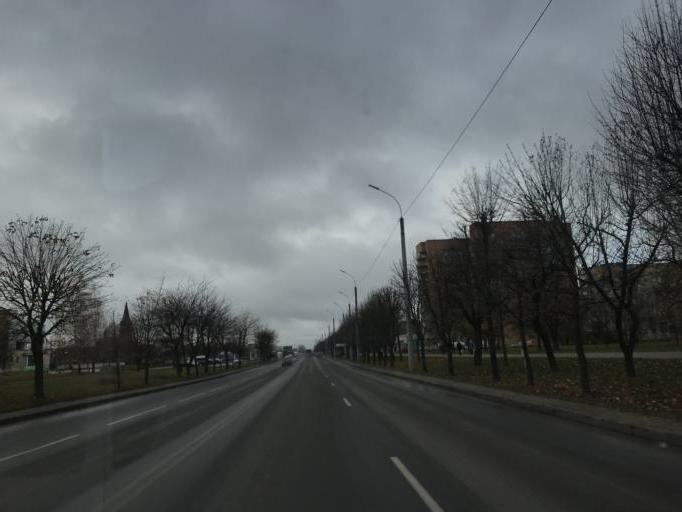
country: BY
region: Mogilev
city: Mahilyow
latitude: 53.8722
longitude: 30.3270
